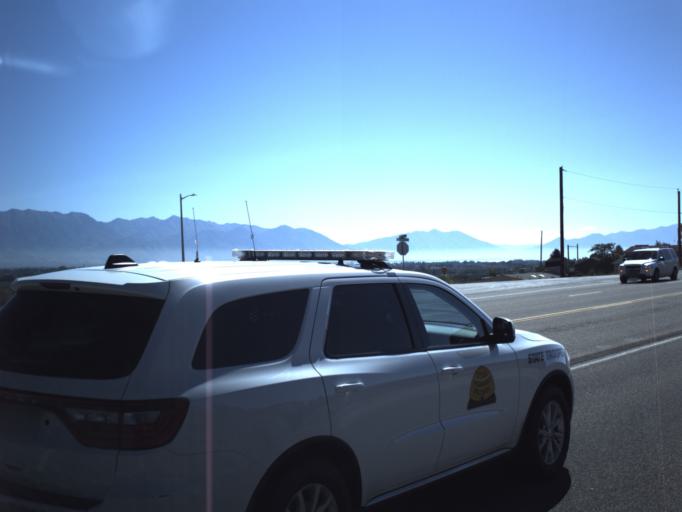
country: US
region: Utah
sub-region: Utah County
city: Saratoga Springs
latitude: 40.4102
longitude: -111.9224
